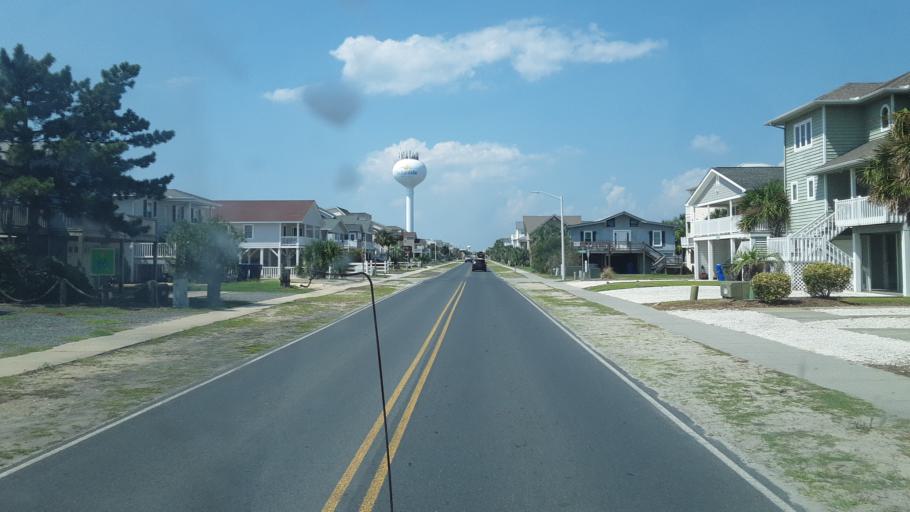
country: US
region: North Carolina
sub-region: Brunswick County
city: Sunset Beach
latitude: 33.8903
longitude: -78.4290
